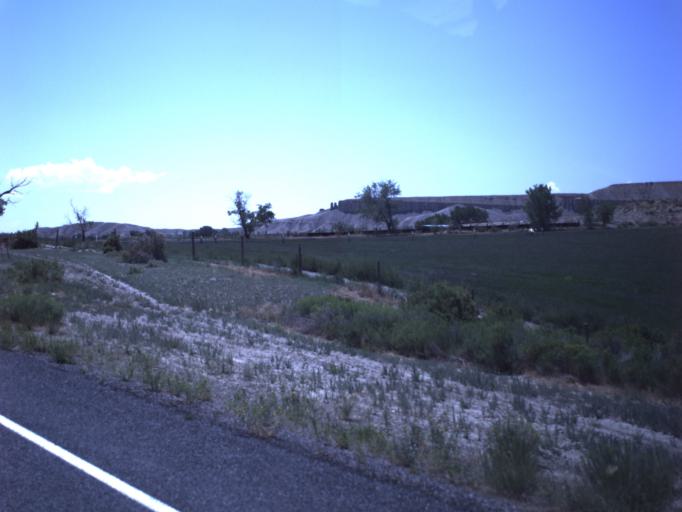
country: US
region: Utah
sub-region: Emery County
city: Orangeville
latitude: 39.2274
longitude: -111.0728
